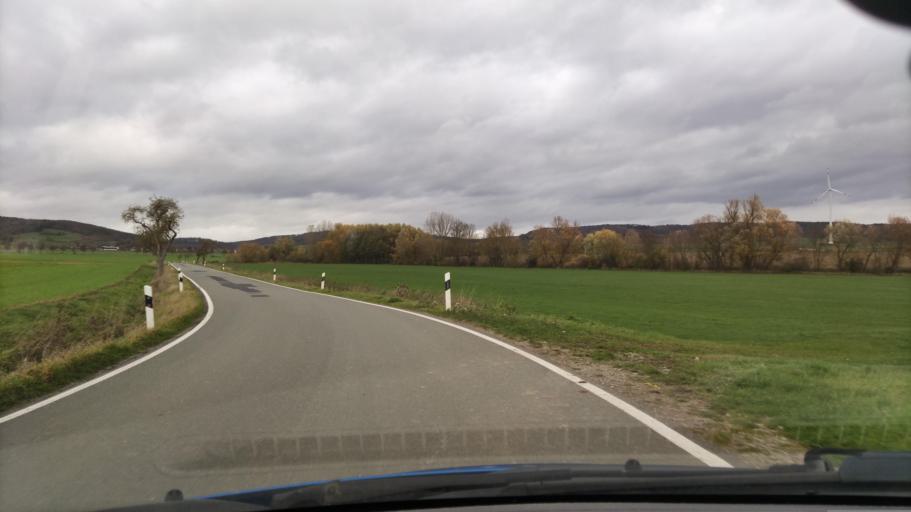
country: DE
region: Lower Saxony
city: Dassel
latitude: 51.8296
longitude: 9.7301
